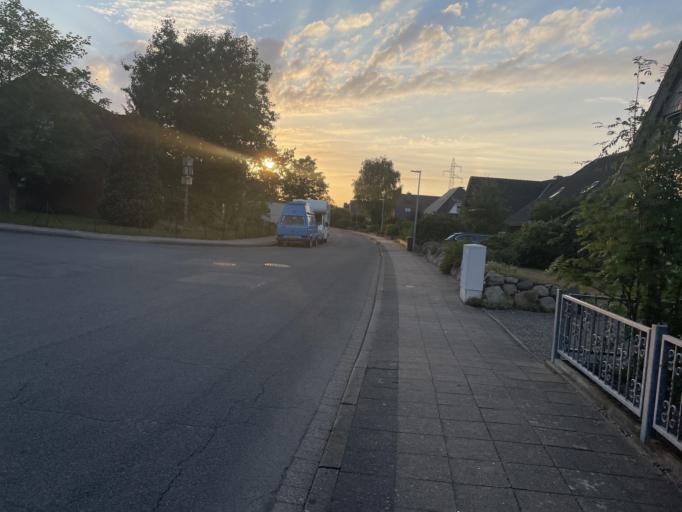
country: DE
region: Schleswig-Holstein
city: Mildstedt
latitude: 54.4733
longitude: 9.0937
